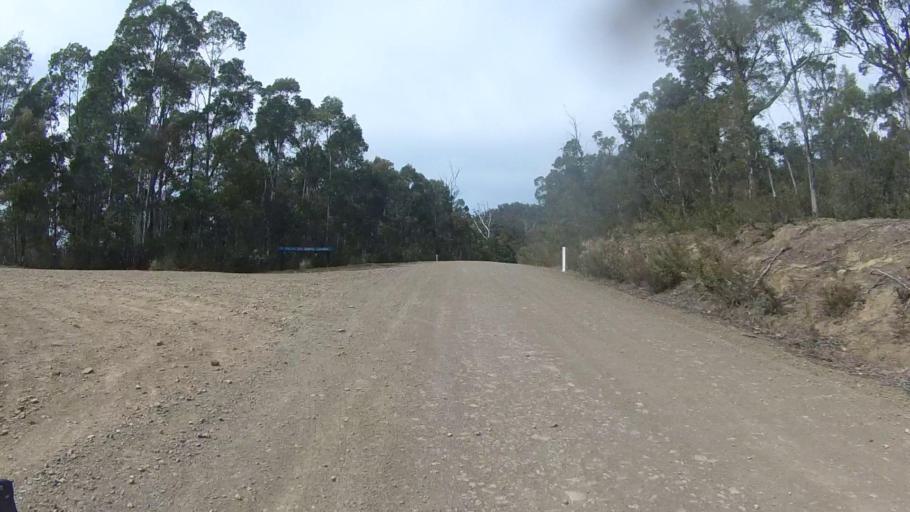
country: AU
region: Tasmania
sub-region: Sorell
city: Sorell
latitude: -42.7580
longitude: 147.8295
